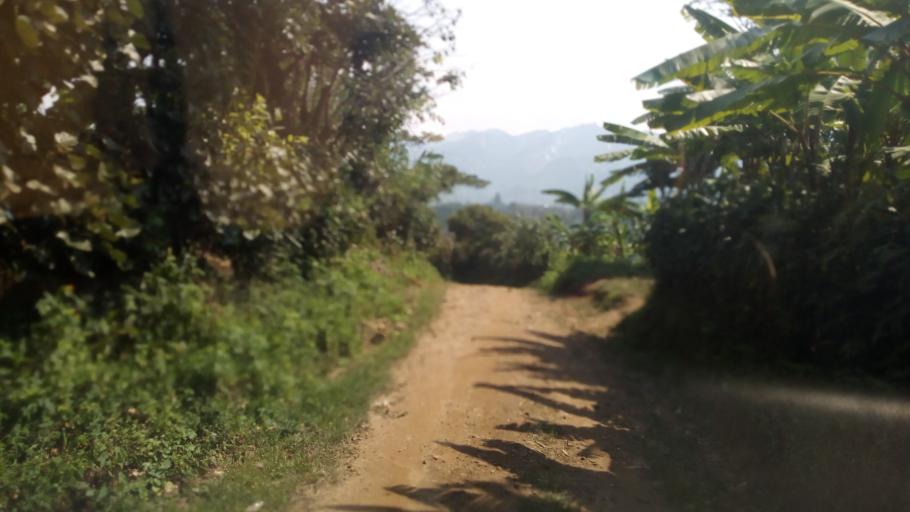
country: UG
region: Western Region
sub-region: Kisoro District
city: Kisoro
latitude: -1.1059
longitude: 29.5921
